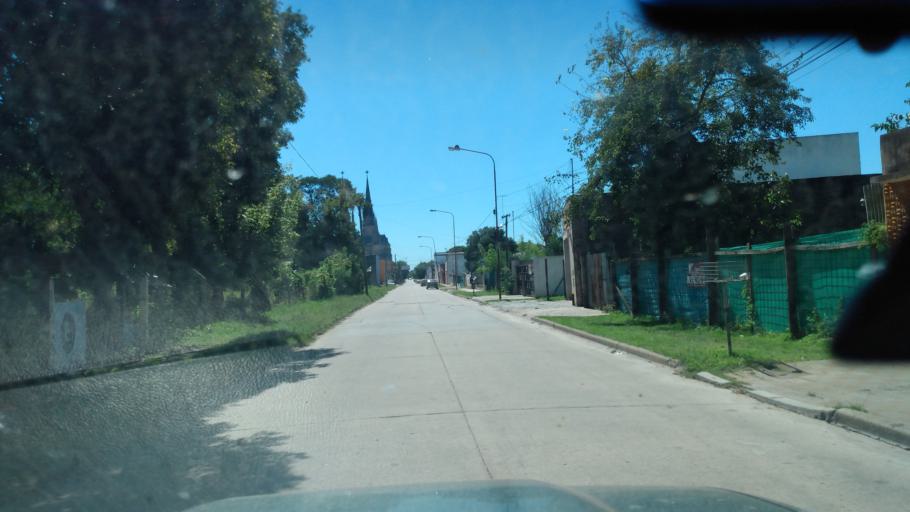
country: AR
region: Buenos Aires
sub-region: Partido de Lujan
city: Lujan
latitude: -34.5702
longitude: -59.1233
